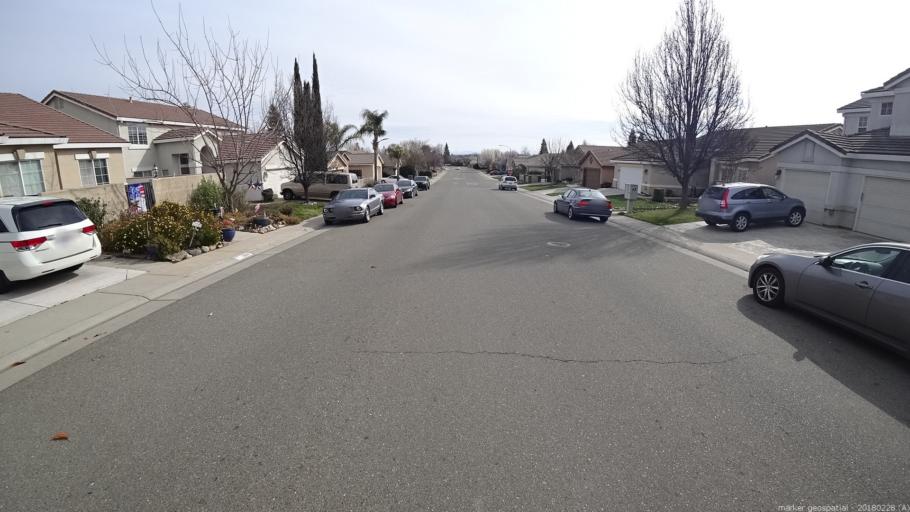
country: US
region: California
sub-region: Sacramento County
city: Antelope
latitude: 38.7221
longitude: -121.3349
